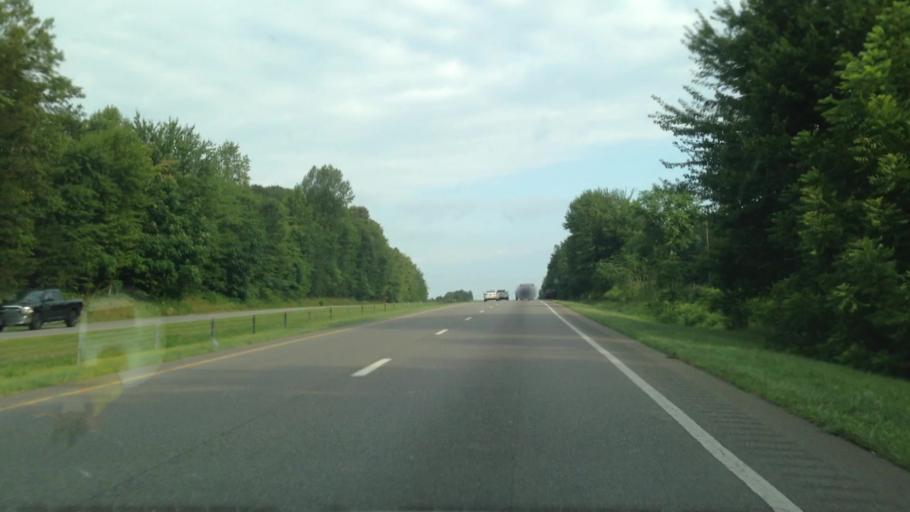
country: US
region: North Carolina
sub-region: Surry County
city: Pilot Mountain
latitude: 36.4266
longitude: -80.5212
